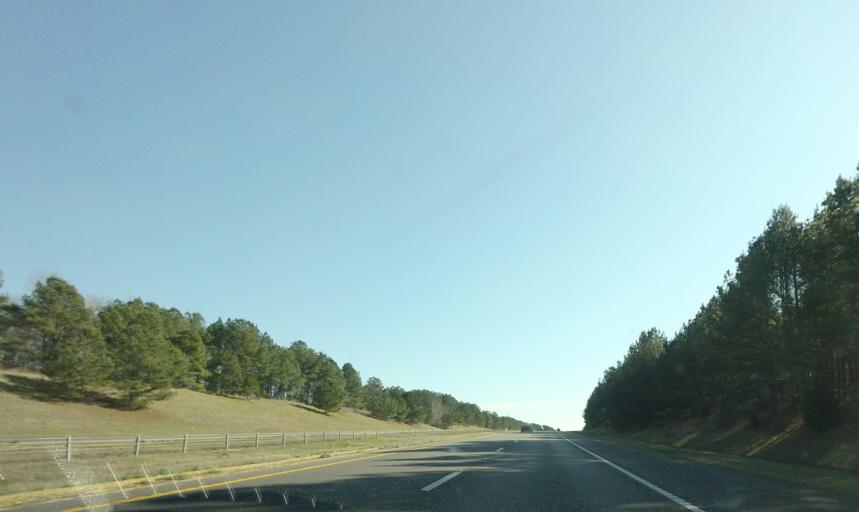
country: US
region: Mississippi
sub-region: Union County
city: New Albany
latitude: 34.5886
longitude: -89.1691
